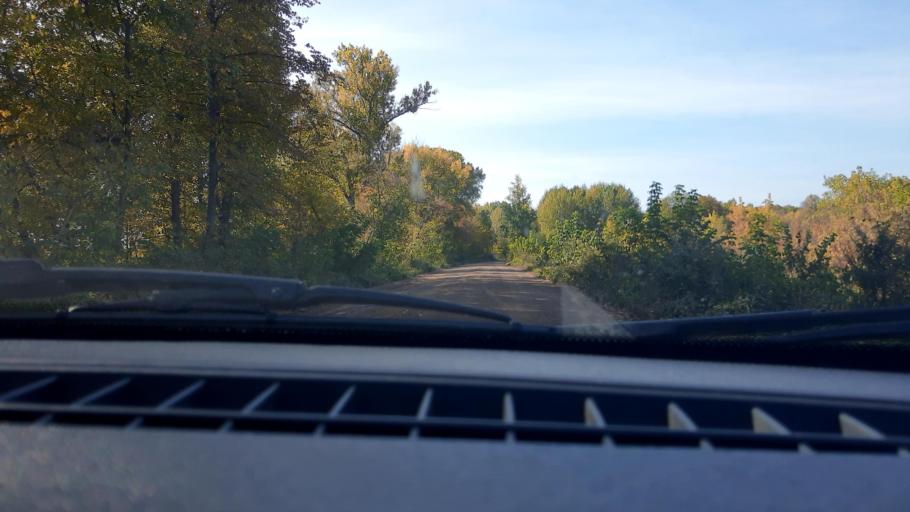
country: RU
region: Bashkortostan
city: Mikhaylovka
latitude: 54.7416
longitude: 55.8544
